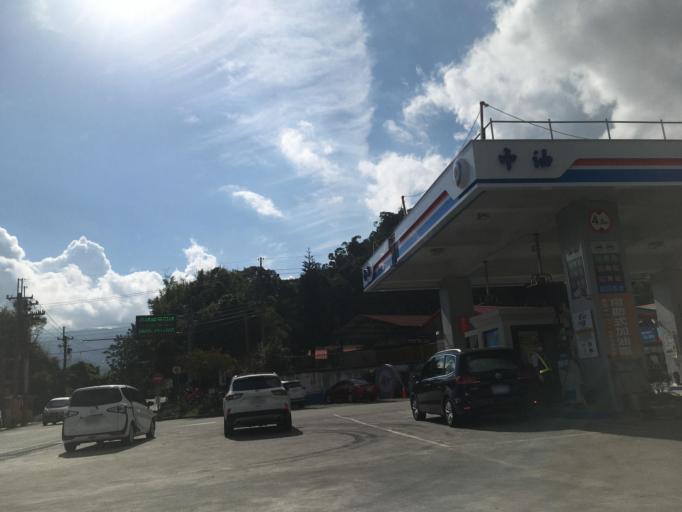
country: TW
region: Taiwan
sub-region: Yilan
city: Yilan
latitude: 24.6713
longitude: 121.6046
